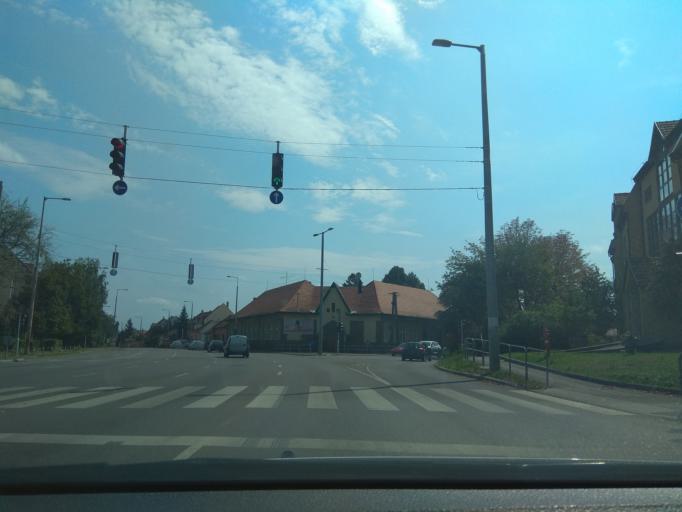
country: HU
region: Heves
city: Eger
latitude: 47.8932
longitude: 20.3713
